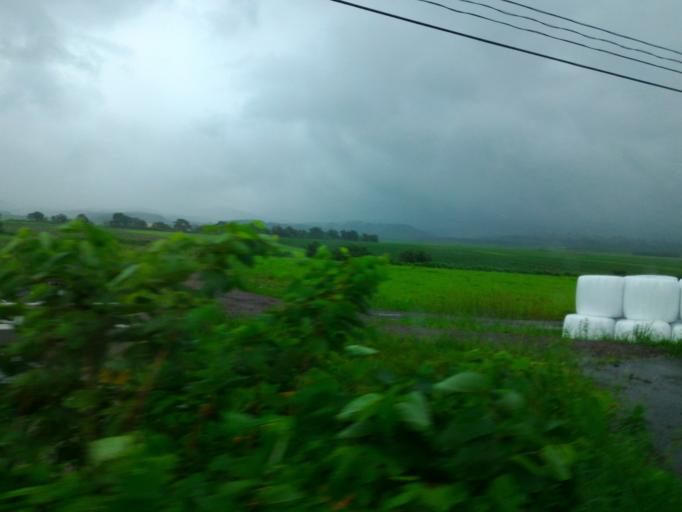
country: JP
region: Hokkaido
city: Makubetsu
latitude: 44.8335
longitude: 142.0575
